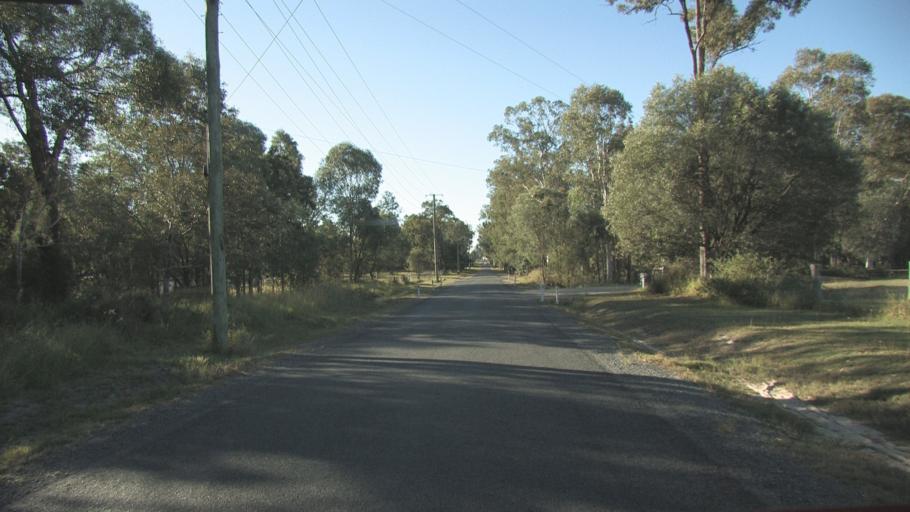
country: AU
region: Queensland
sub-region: Logan
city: Chambers Flat
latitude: -27.7841
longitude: 153.0867
